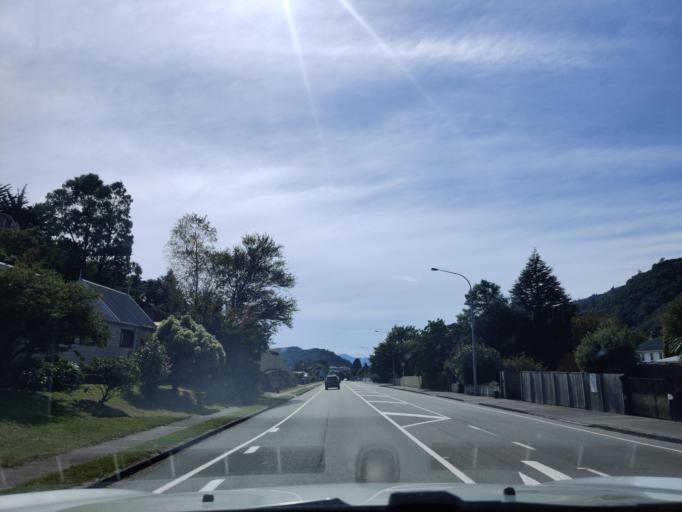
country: NZ
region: Marlborough
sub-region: Marlborough District
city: Picton
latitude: -41.2994
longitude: 173.9985
